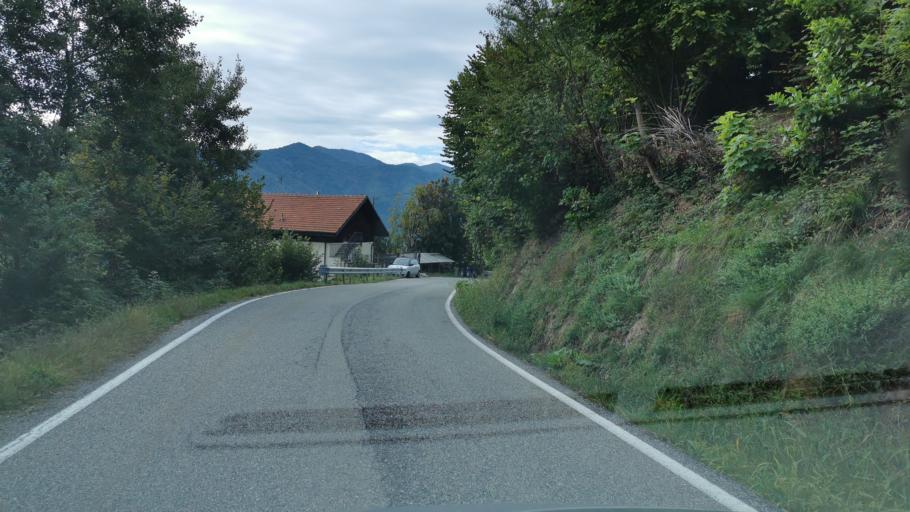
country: IT
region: Piedmont
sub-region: Provincia di Torino
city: Lanzo Torinese
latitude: 45.2917
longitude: 7.4821
